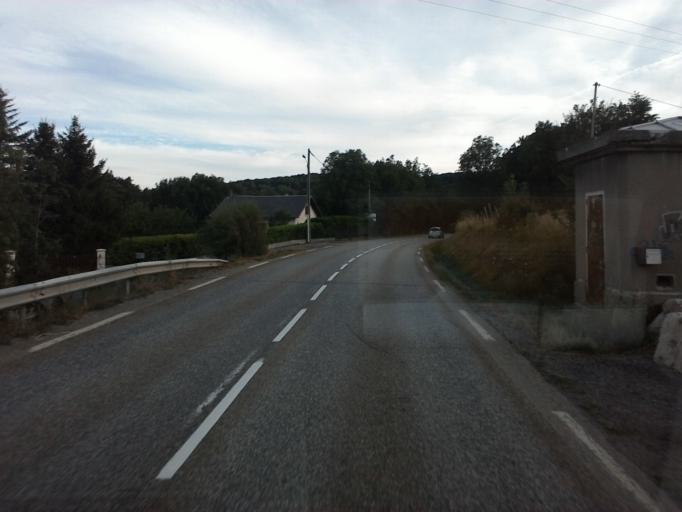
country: FR
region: Rhone-Alpes
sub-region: Departement de l'Isere
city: La Mure
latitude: 44.8724
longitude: 5.8389
